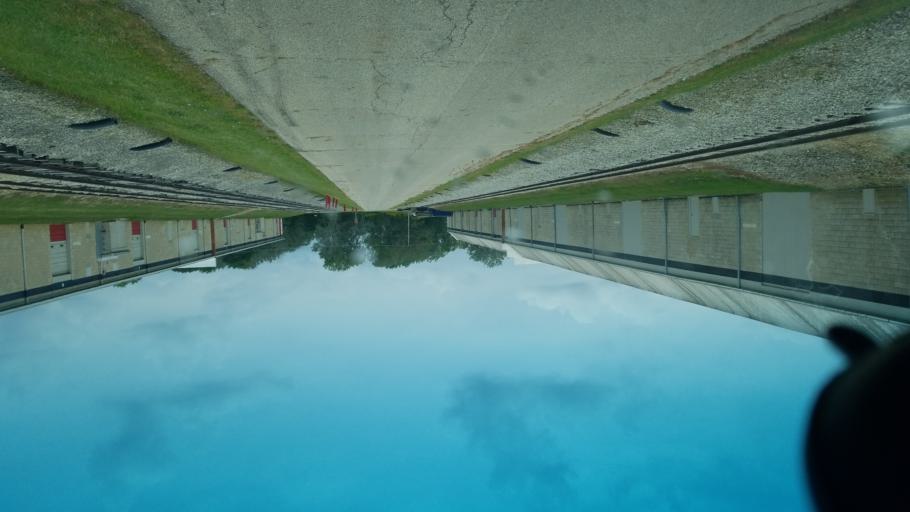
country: US
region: Ohio
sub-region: Richland County
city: Shelby
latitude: 40.8988
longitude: -82.6737
